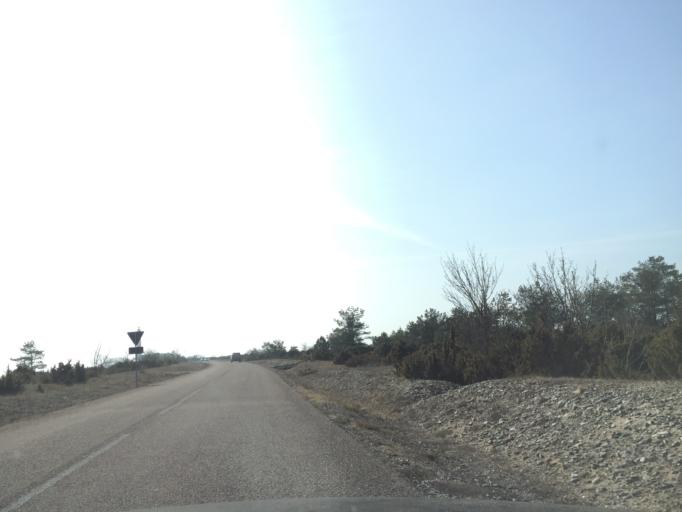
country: LV
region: Dundaga
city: Dundaga
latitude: 57.9170
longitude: 22.0626
